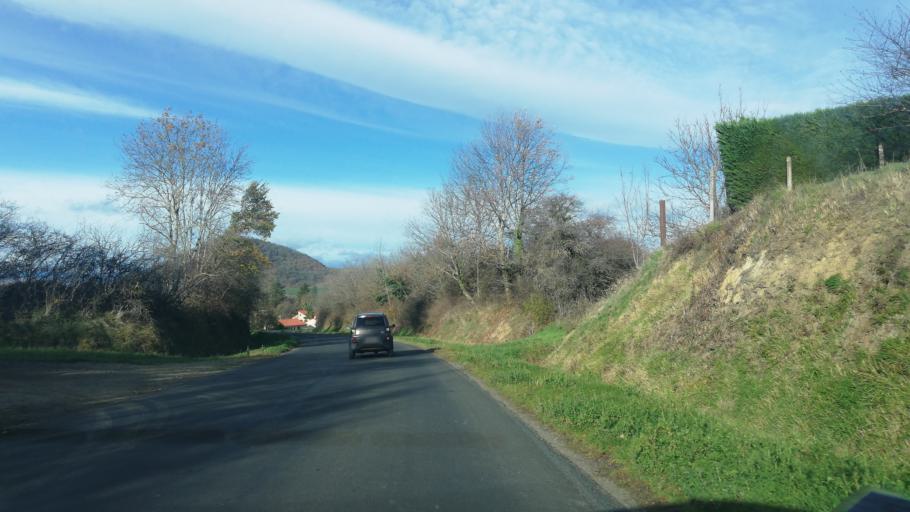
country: FR
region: Auvergne
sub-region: Departement du Puy-de-Dome
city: Billom
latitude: 45.7157
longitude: 3.3459
